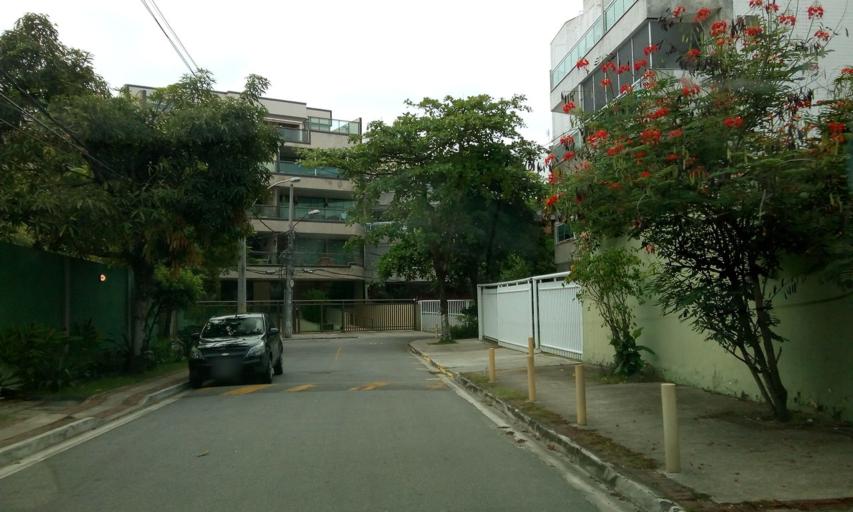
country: BR
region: Rio de Janeiro
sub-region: Nilopolis
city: Nilopolis
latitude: -23.0162
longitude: -43.4532
